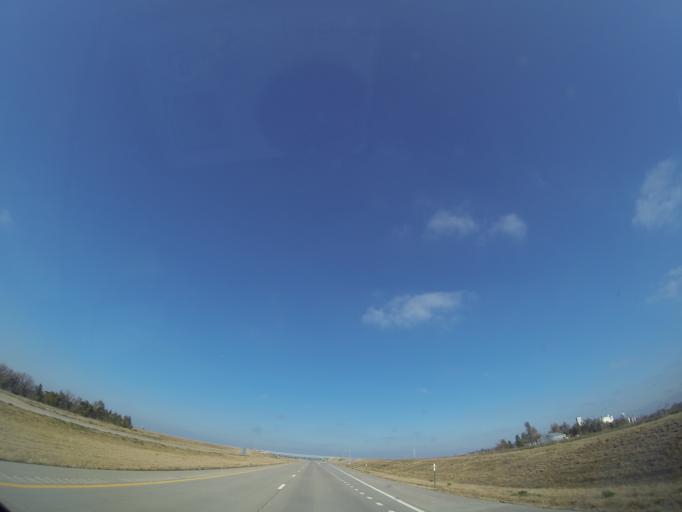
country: US
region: Kansas
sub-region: McPherson County
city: Inman
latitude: 38.2275
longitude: -97.7848
